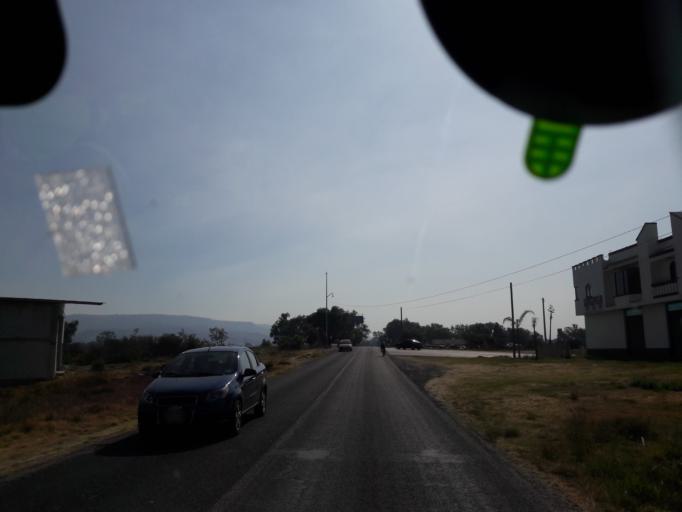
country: MX
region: Tlaxcala
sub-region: Ixtacuixtla de Mariano Matamoros
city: Santa Justina Ecatepec
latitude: 19.3138
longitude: -98.3343
